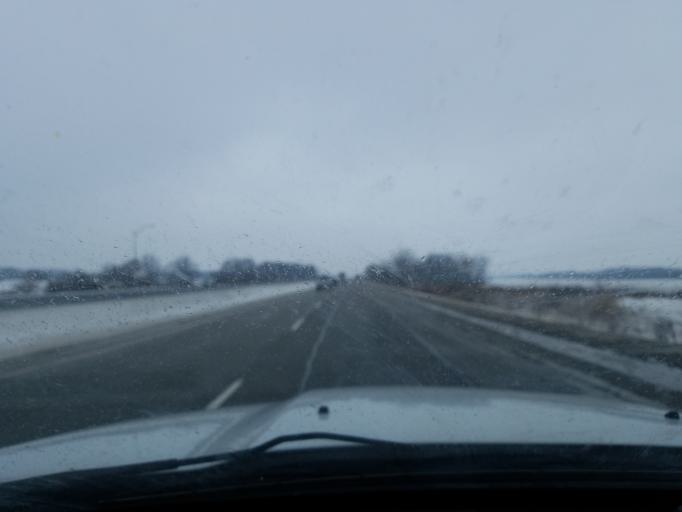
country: US
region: Indiana
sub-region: Marshall County
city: Argos
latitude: 41.1729
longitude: -86.2420
